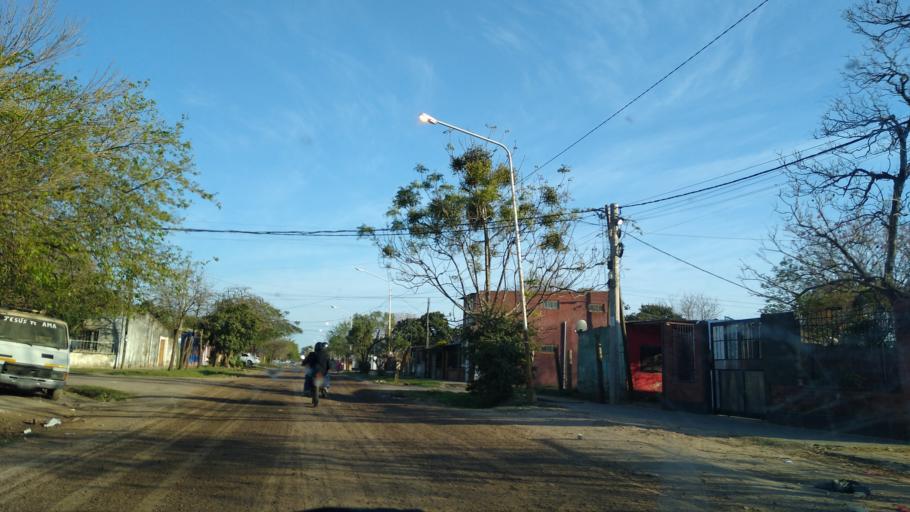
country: AR
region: Chaco
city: Barranqueras
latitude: -27.4736
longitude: -58.9307
